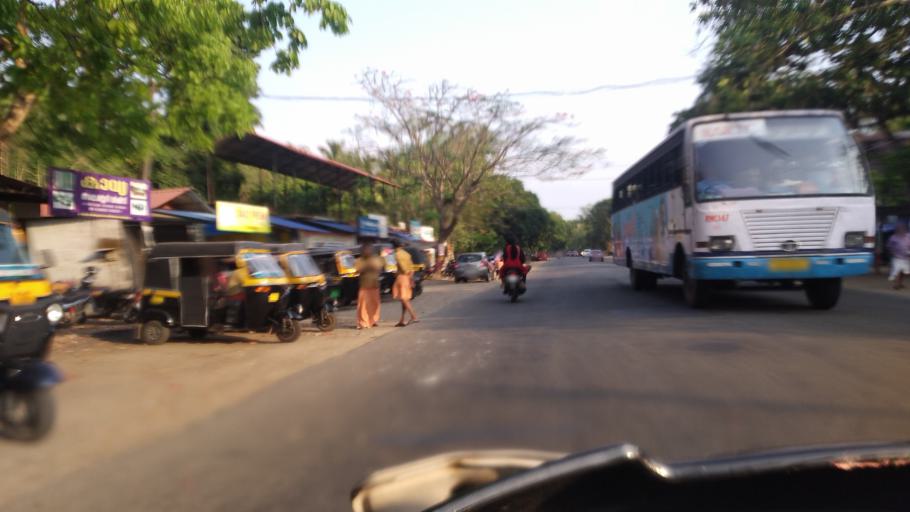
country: IN
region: Kerala
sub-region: Thrissur District
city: Thanniyam
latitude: 10.4402
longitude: 76.0949
